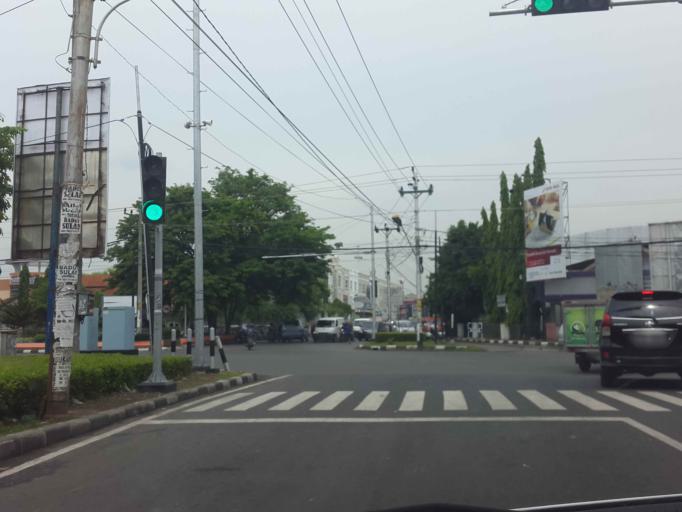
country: ID
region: Central Java
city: Semarang
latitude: -7.0003
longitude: 110.4449
